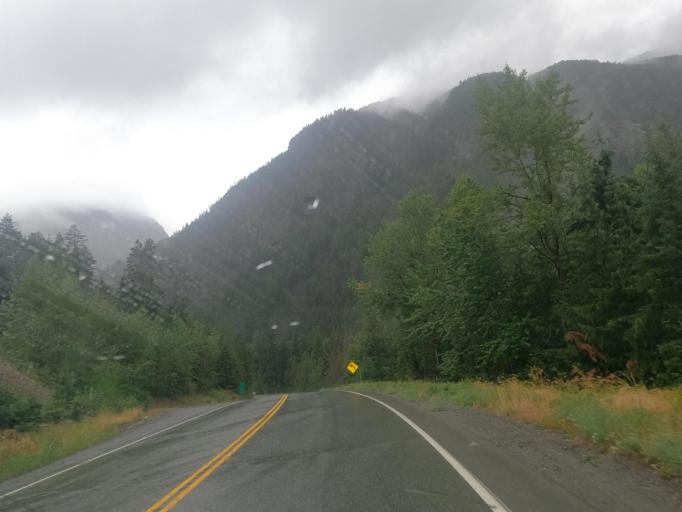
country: CA
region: British Columbia
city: Lillooet
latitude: 50.5347
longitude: -122.1404
